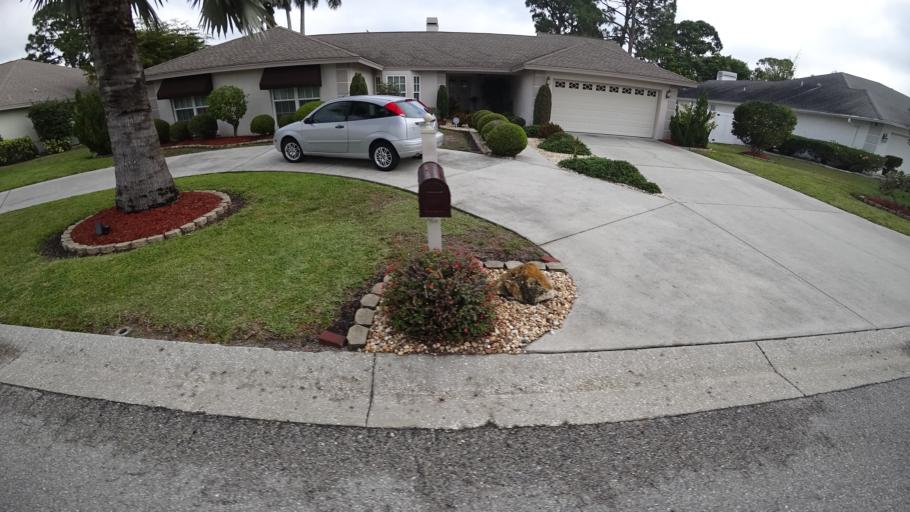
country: US
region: Florida
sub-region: Manatee County
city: Bayshore Gardens
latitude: 27.4327
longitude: -82.5989
